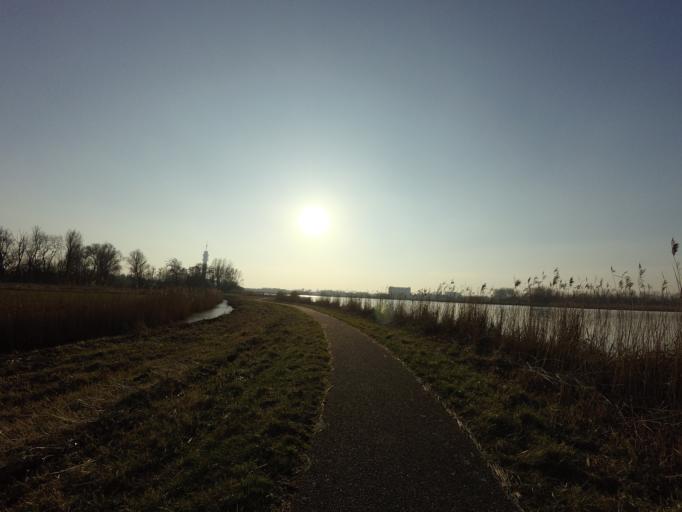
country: NL
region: North Holland
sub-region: Gemeente Haarlem
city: Haarlem
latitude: 52.3955
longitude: 4.6760
